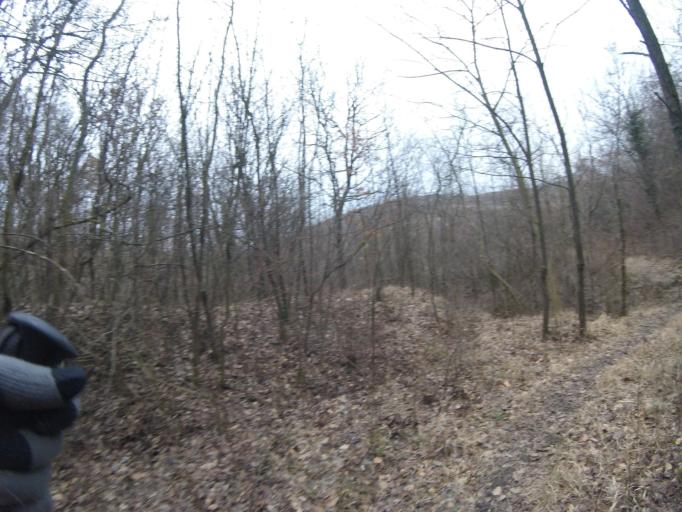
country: HU
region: Komarom-Esztergom
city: Kesztolc
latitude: 47.7147
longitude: 18.8131
